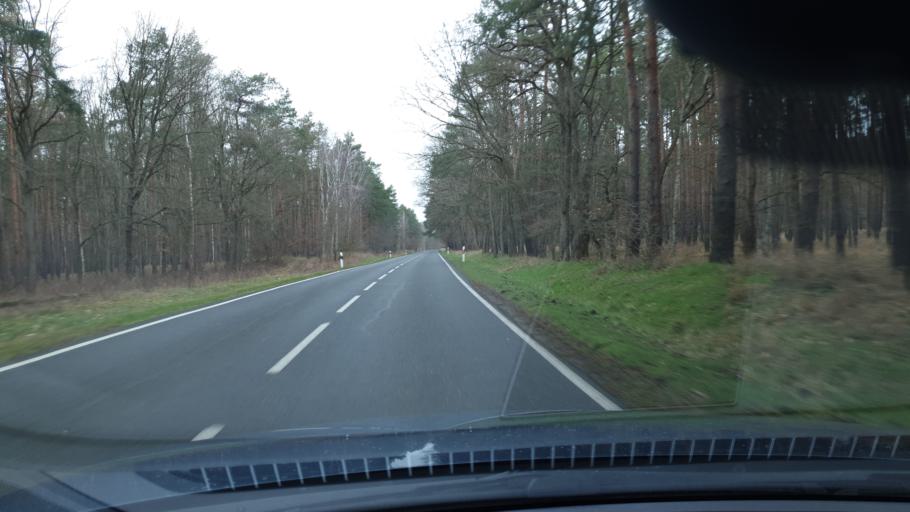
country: DE
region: Saxony-Anhalt
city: Radis
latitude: 51.7636
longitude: 12.4990
